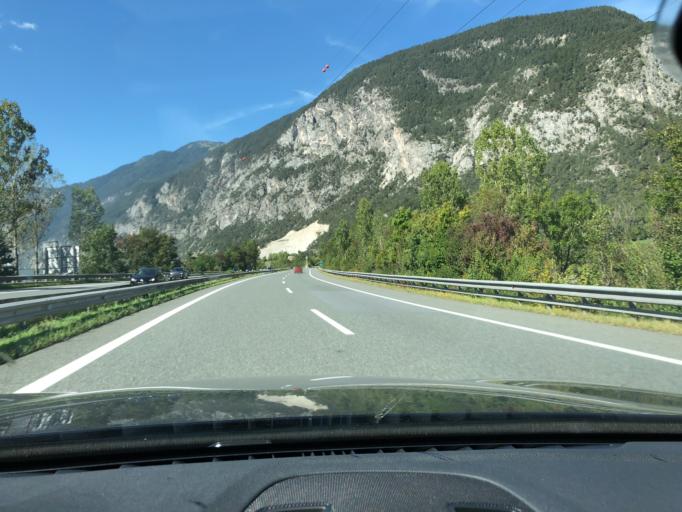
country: AT
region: Tyrol
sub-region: Politischer Bezirk Imst
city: Motz
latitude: 47.2724
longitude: 10.9486
